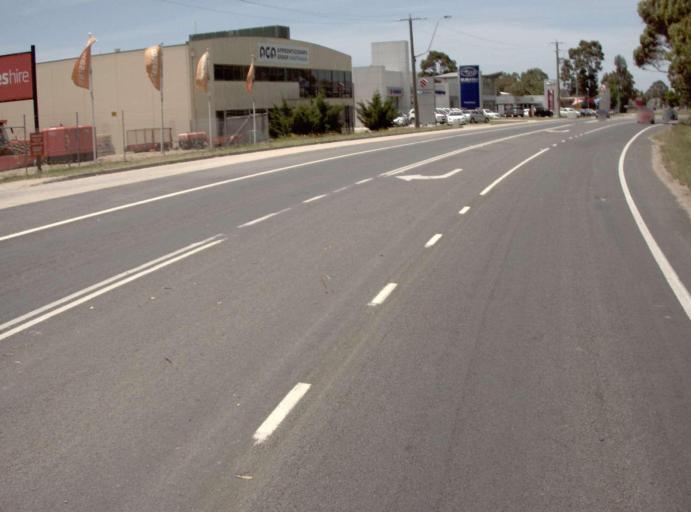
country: AU
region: Victoria
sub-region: East Gippsland
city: Bairnsdale
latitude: -37.8394
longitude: 147.5938
